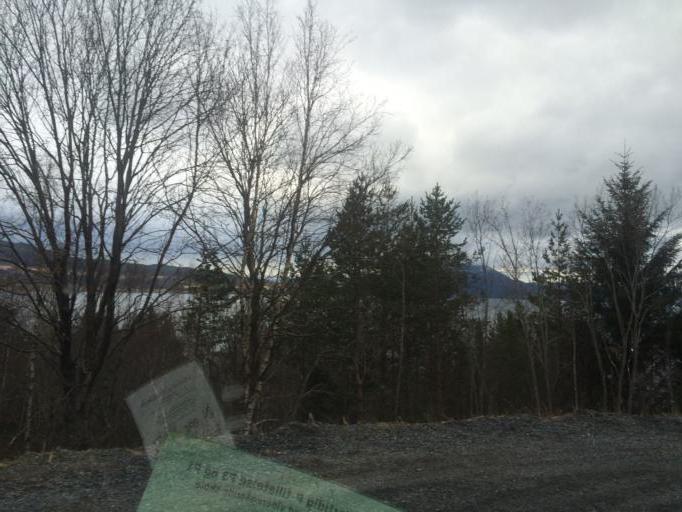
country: NO
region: More og Romsdal
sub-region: Gjemnes
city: Batnfjordsora
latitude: 62.9666
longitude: 7.7268
